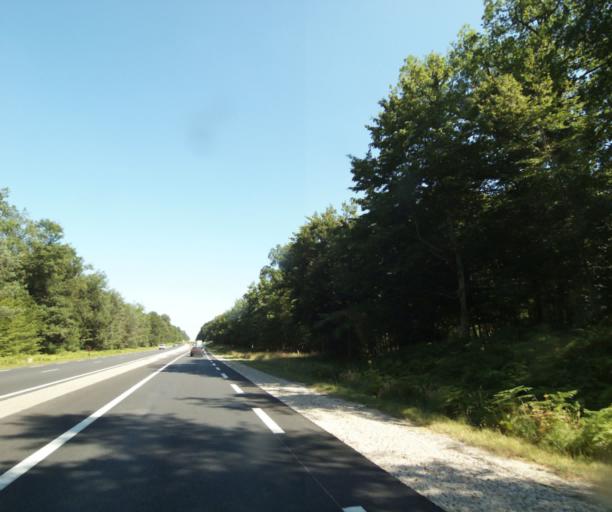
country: FR
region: Ile-de-France
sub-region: Departement de Seine-et-Marne
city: Avon
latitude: 48.3926
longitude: 2.7496
